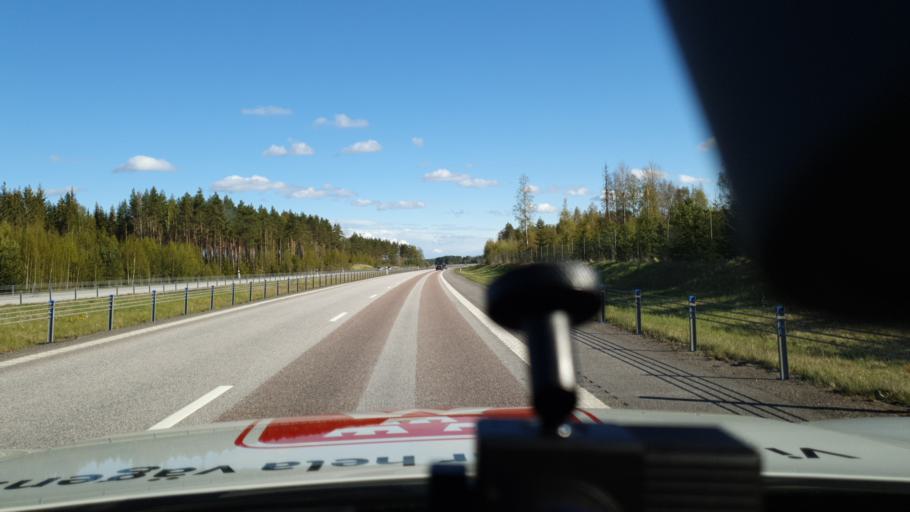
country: SE
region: Uppsala
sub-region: Osthammars Kommun
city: Bjorklinge
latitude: 60.0804
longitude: 17.5998
